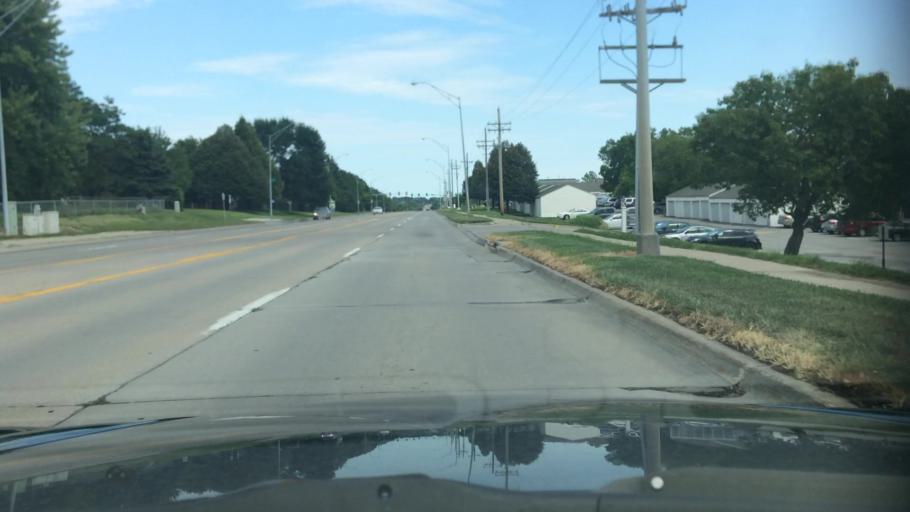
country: US
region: Nebraska
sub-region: Douglas County
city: Ralston
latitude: 41.2053
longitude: -96.0714
